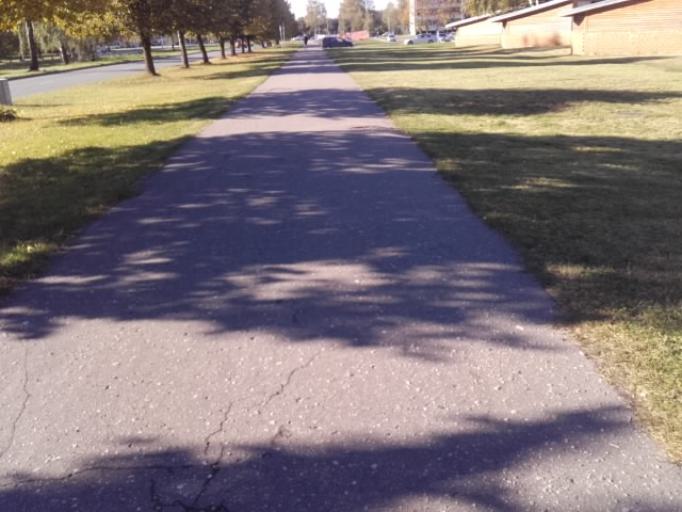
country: LV
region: Stopini
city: Ulbroka
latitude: 56.9405
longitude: 24.1995
